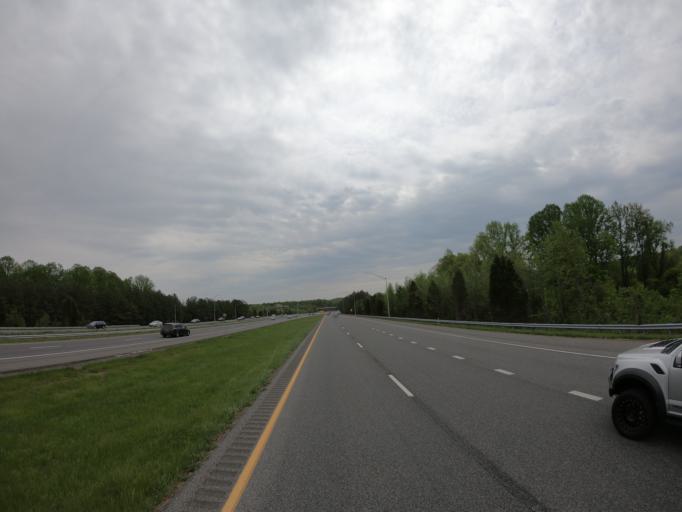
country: US
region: Maryland
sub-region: Anne Arundel County
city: Gambrills
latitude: 39.0599
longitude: -76.6369
